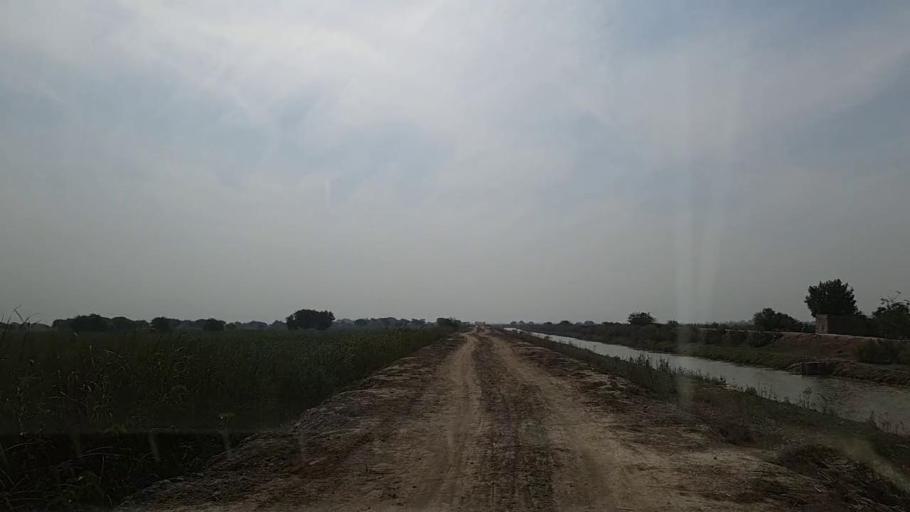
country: PK
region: Sindh
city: Mirpur Batoro
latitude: 24.6674
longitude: 68.2501
